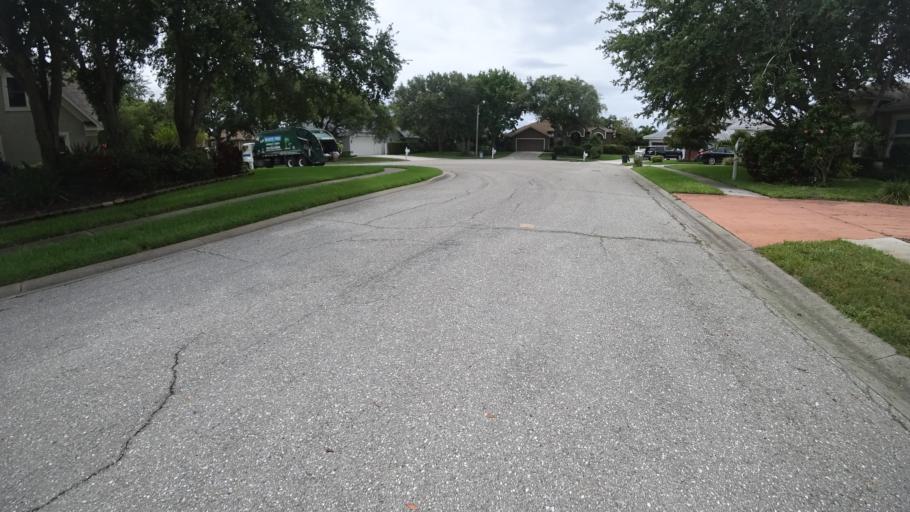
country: US
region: Florida
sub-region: Manatee County
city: West Bradenton
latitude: 27.5170
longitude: -82.6552
